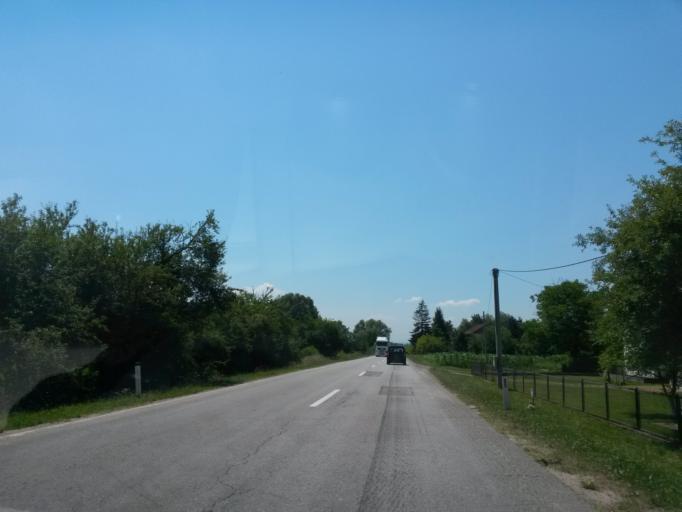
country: BA
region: Federation of Bosnia and Herzegovina
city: Lukavica
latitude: 44.9264
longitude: 18.1101
